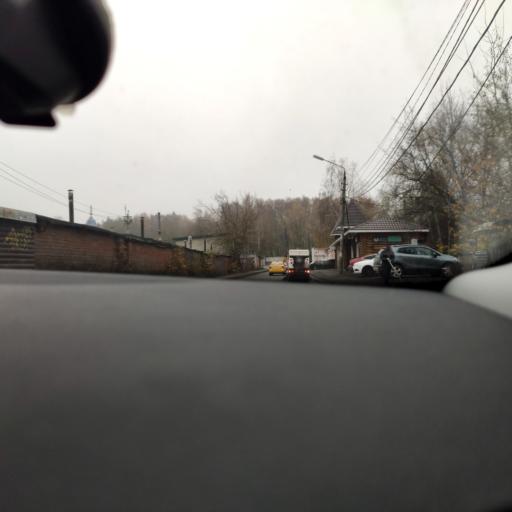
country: RU
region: Moskovskaya
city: Nakhabino
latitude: 55.8439
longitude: 37.1567
